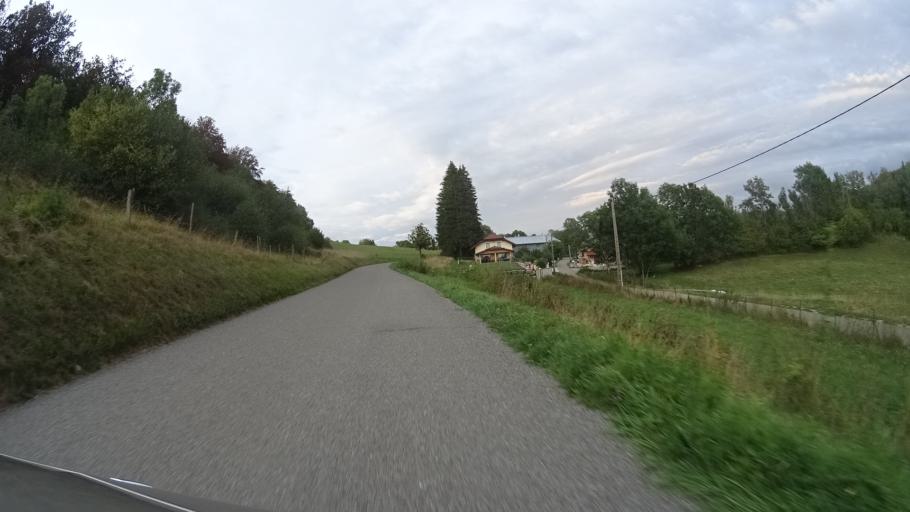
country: FR
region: Franche-Comte
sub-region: Departement du Jura
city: Morbier
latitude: 46.6149
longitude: 5.9755
